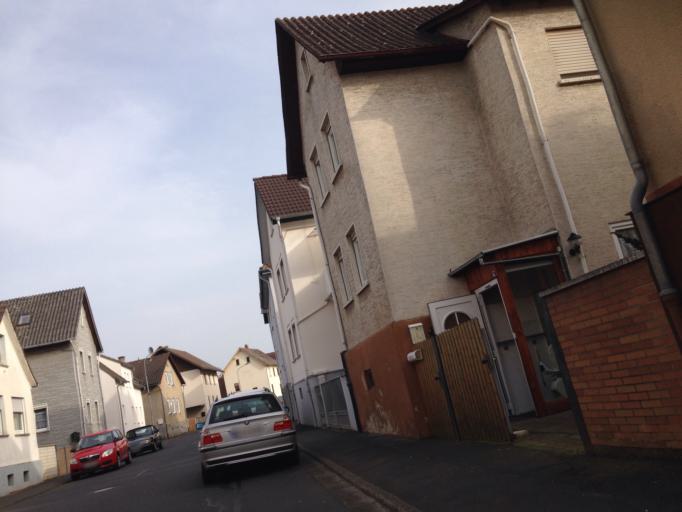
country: DE
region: Hesse
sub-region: Regierungsbezirk Giessen
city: Grossen Buseck
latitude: 50.6051
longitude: 8.7904
